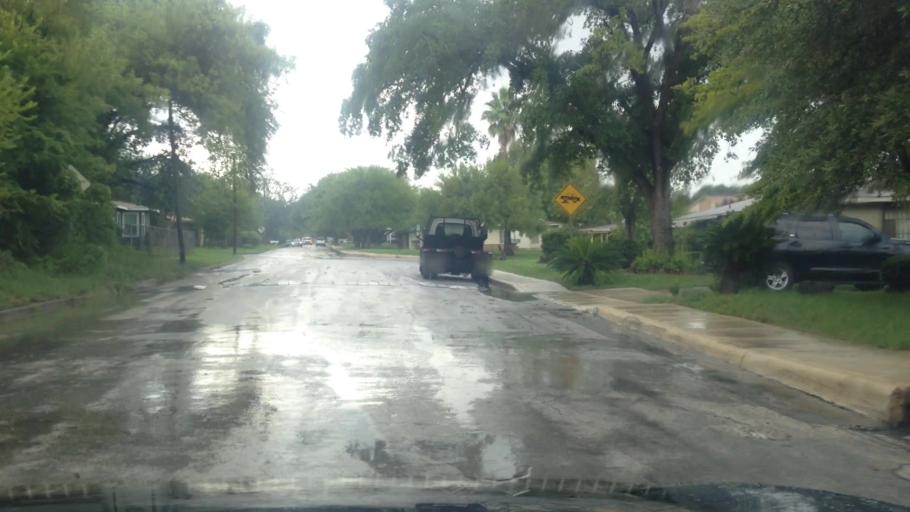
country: US
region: Texas
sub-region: Bexar County
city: Balcones Heights
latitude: 29.4807
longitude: -98.5463
